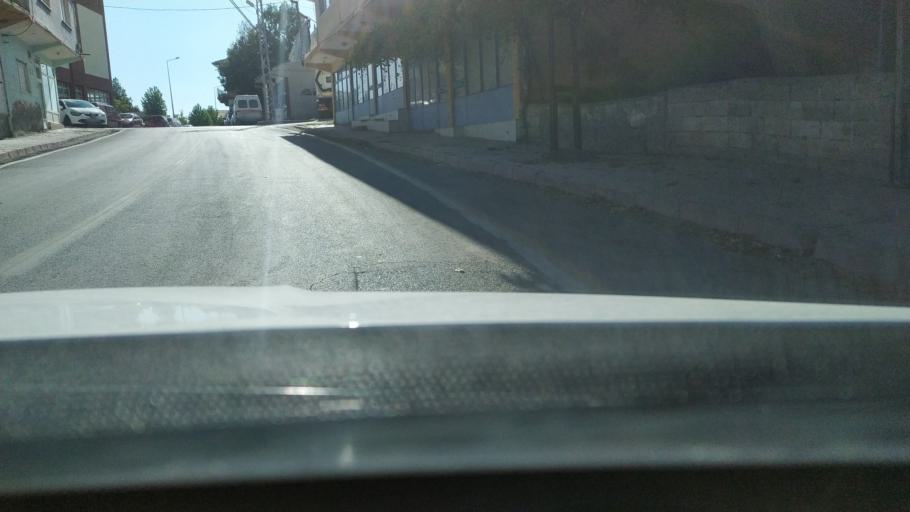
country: TR
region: Kayseri
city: Felahiye
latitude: 39.0927
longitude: 35.5678
